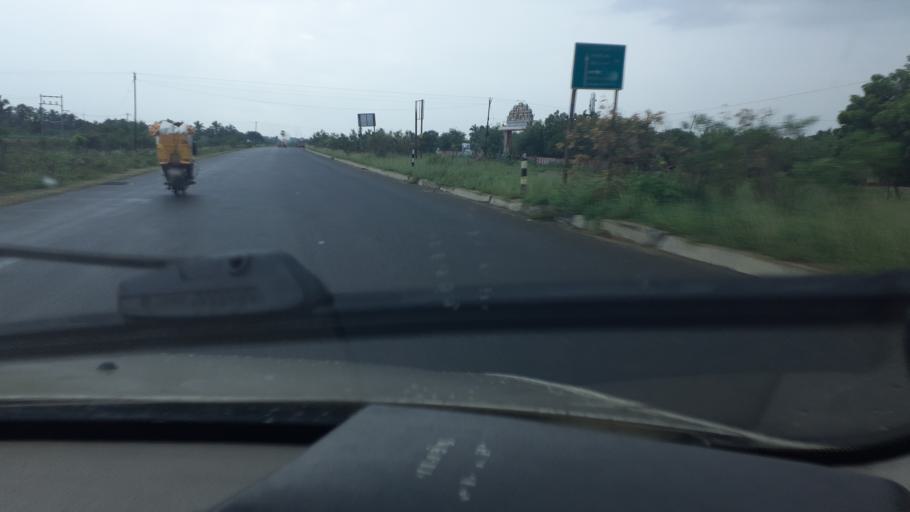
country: IN
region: Tamil Nadu
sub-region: Thoothukkudi
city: Kadambur
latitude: 9.0518
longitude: 77.7955
